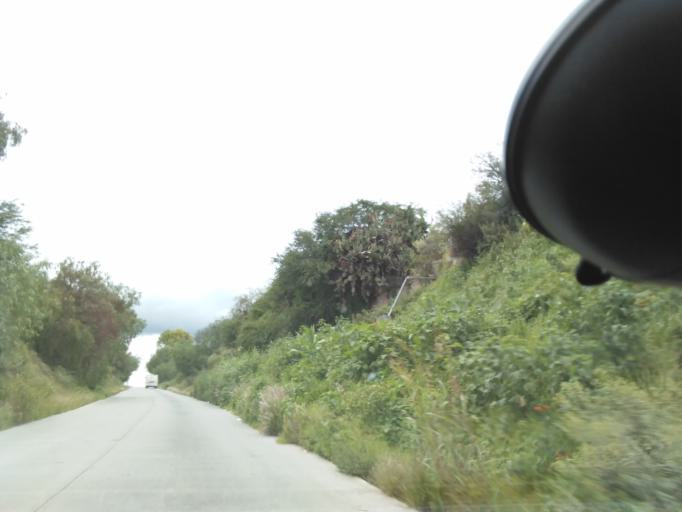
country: MX
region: Hidalgo
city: Tula de Allende
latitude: 20.0592
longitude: -99.3539
